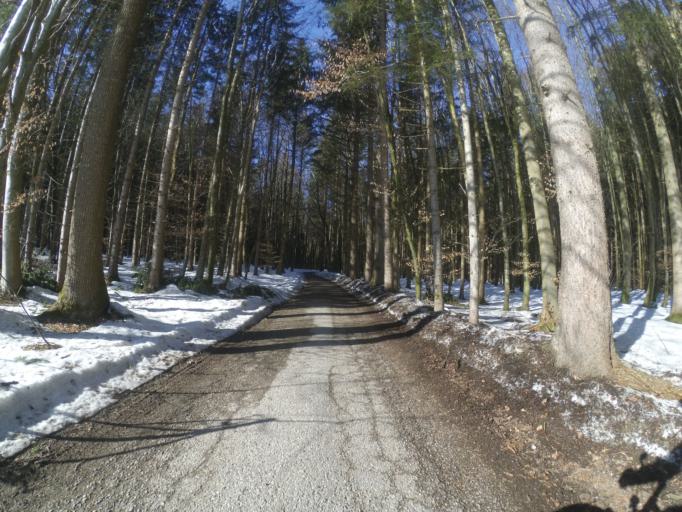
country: DE
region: Bavaria
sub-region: Upper Bavaria
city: Feldkirchen-Westerham
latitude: 47.9340
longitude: 11.8096
